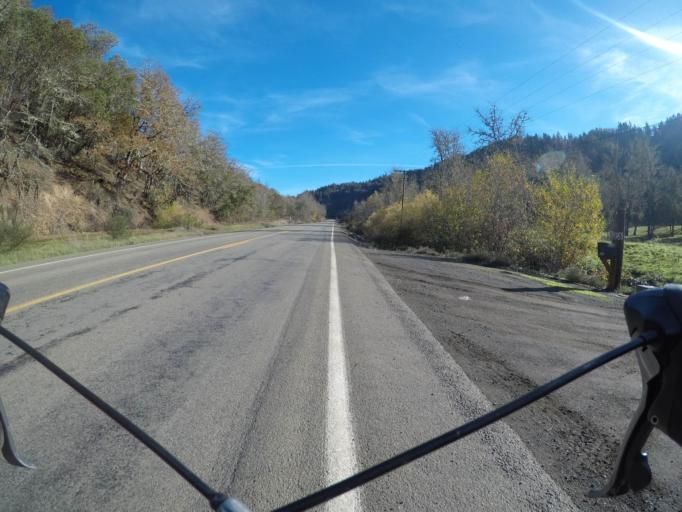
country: US
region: Oregon
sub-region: Douglas County
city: Winston
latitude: 43.1877
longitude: -123.4502
